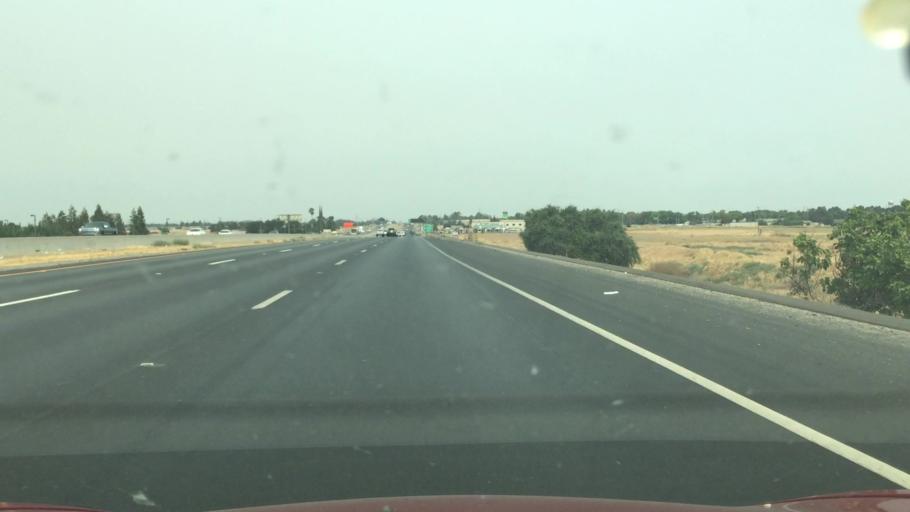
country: US
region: California
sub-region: San Joaquin County
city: French Camp
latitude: 37.8865
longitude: -121.2798
